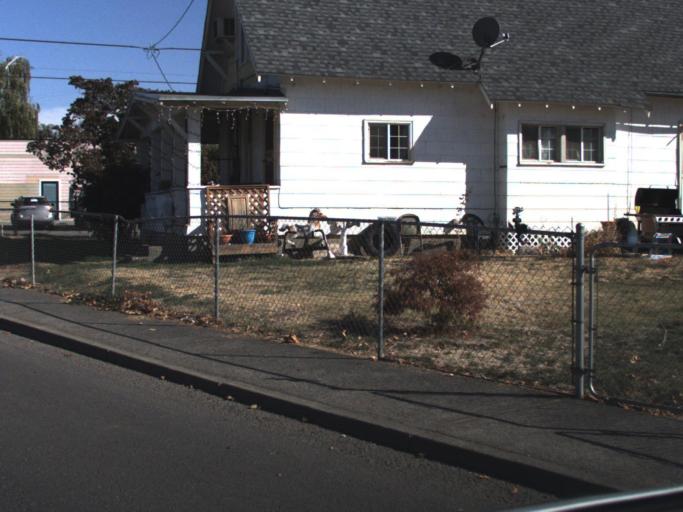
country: US
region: Washington
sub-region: Walla Walla County
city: Walla Walla
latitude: 46.0690
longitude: -118.3551
